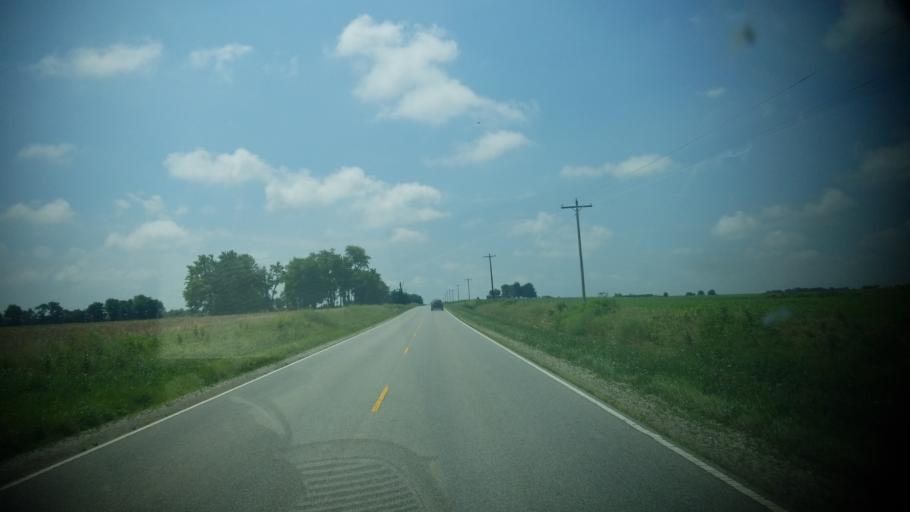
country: US
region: Illinois
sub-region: Wayne County
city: Fairfield
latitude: 38.4413
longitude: -88.3494
